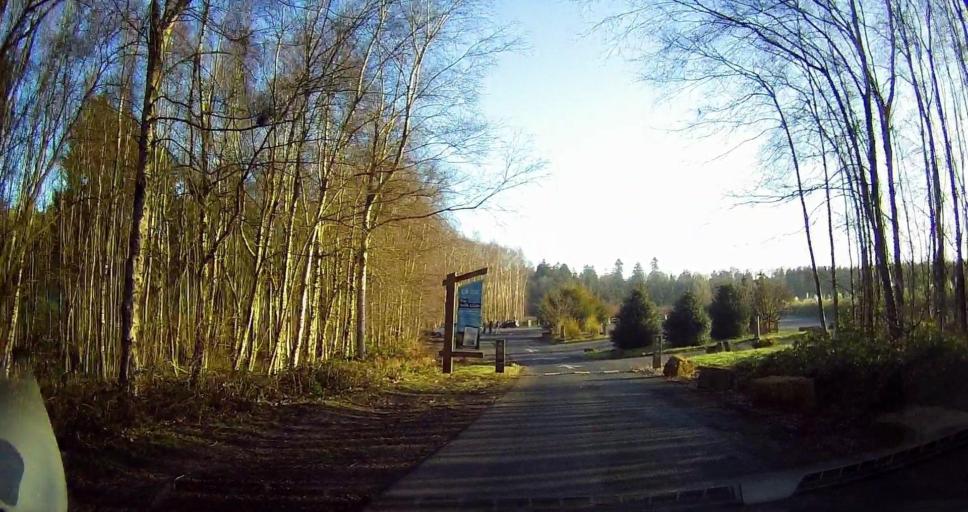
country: GB
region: England
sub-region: Kent
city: Hawkhurst
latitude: 51.0721
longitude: 0.4453
